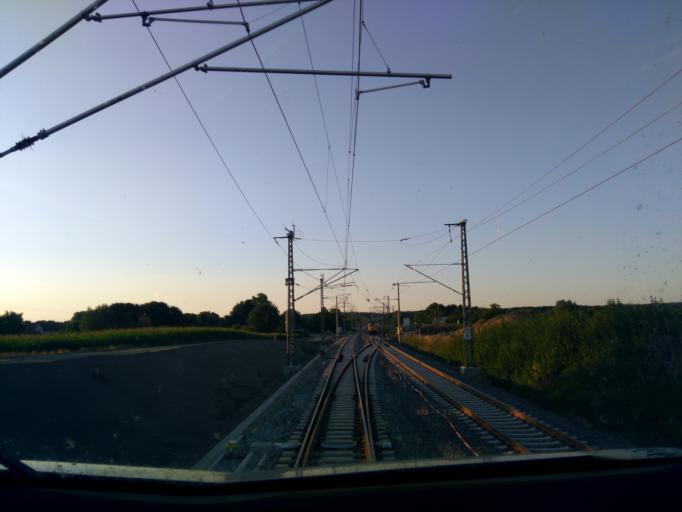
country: DE
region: Mecklenburg-Vorpommern
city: Lubstorf
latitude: 53.7171
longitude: 11.4096
